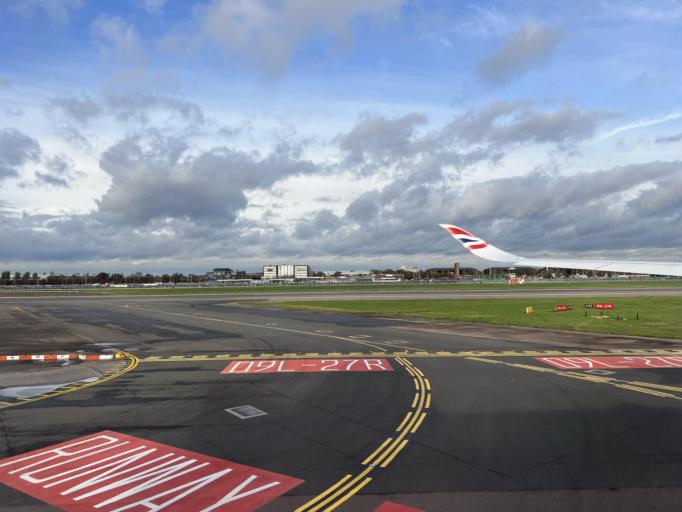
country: GB
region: England
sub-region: Greater London
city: West Drayton
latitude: 51.4760
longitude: -0.4608
